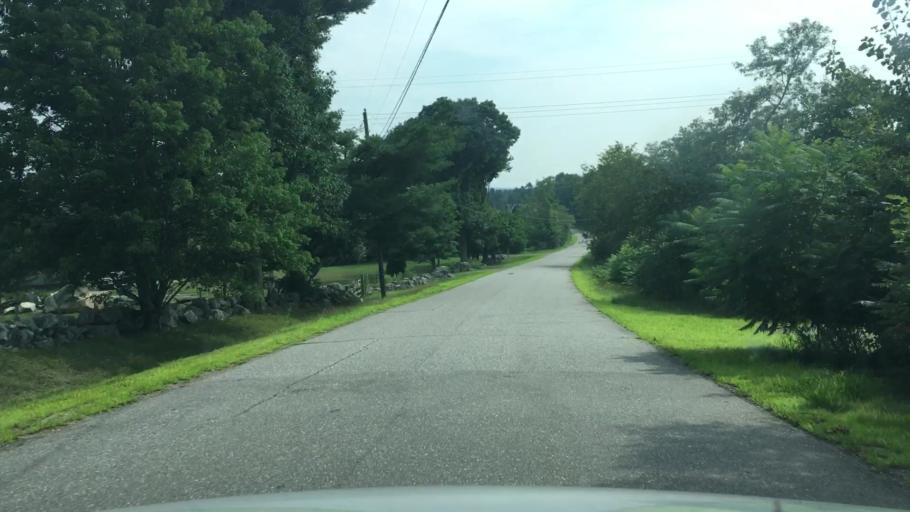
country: US
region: Maine
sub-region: Lincoln County
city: Jefferson
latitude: 44.2259
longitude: -69.4461
